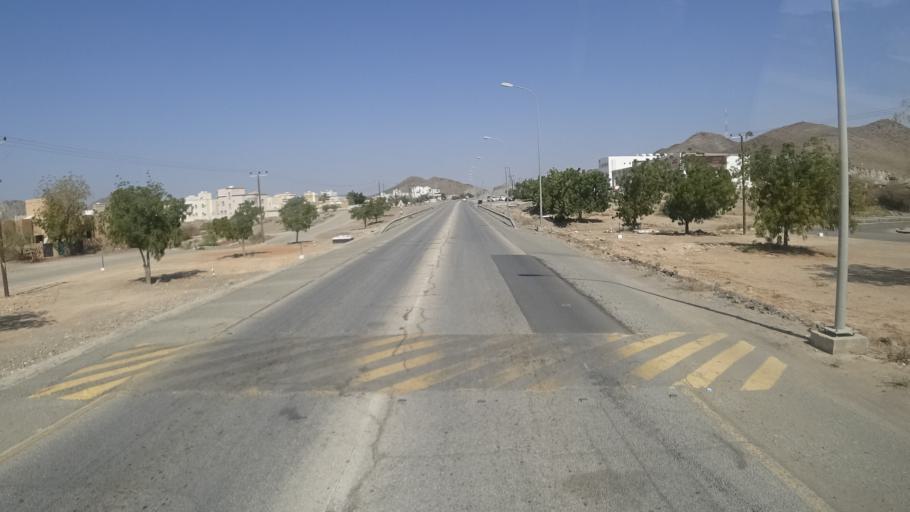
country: OM
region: Ash Sharqiyah
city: Ibra'
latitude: 22.6894
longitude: 58.5516
